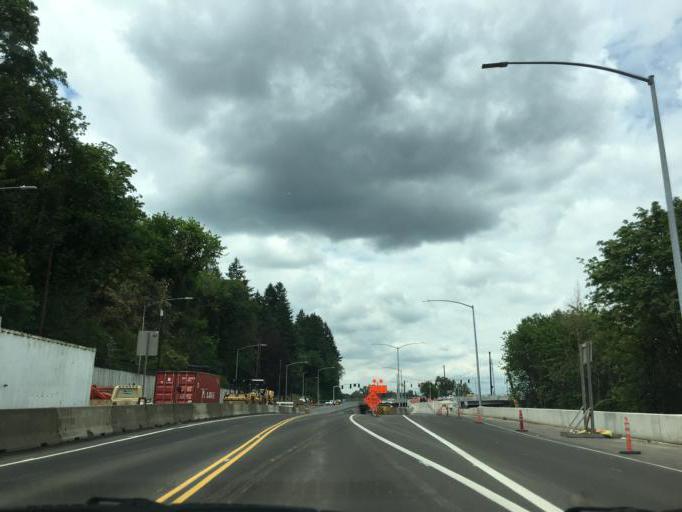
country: US
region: Oregon
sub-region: Clackamas County
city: Milwaukie
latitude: 45.4622
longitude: -122.6684
